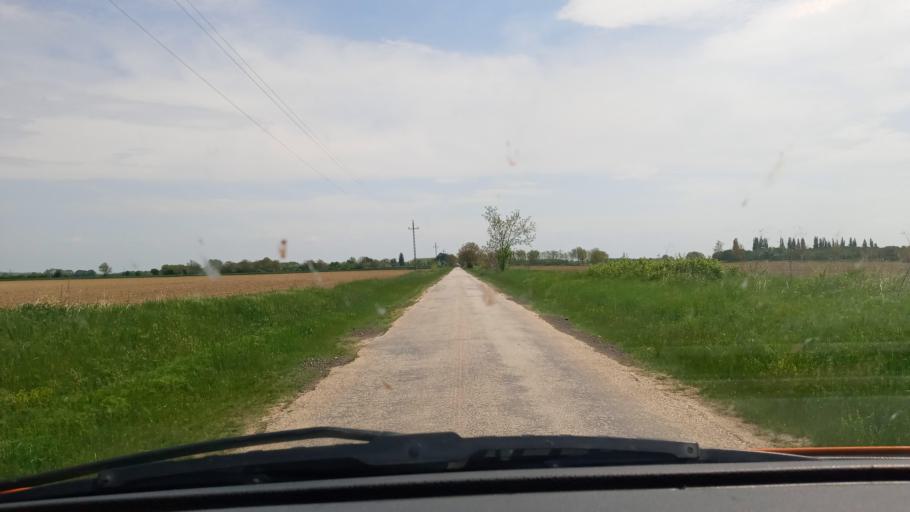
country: HU
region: Baranya
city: Villany
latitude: 45.8128
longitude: 18.5128
